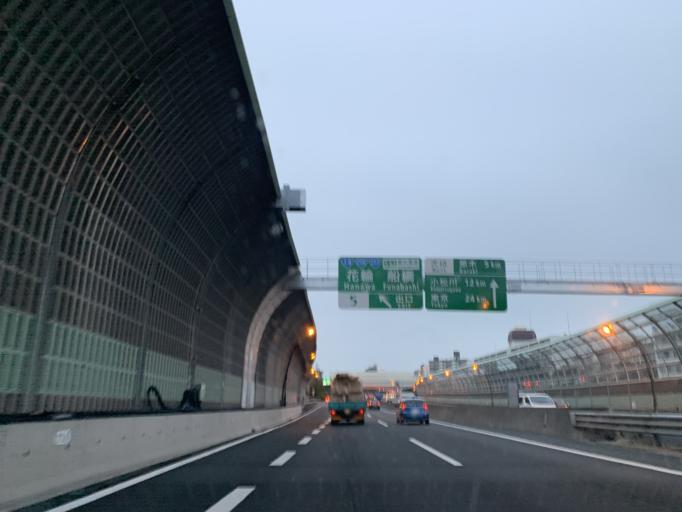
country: JP
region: Chiba
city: Funabashi
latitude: 35.6844
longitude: 140.0046
